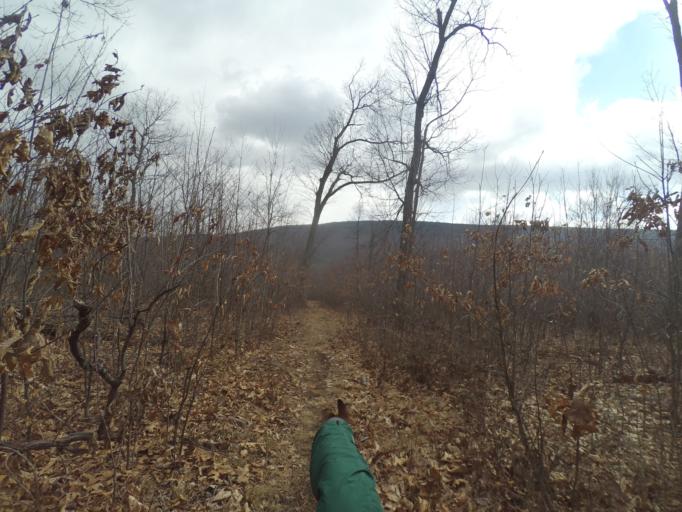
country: US
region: Pennsylvania
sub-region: Centre County
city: Boalsburg
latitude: 40.7595
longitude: -77.7159
